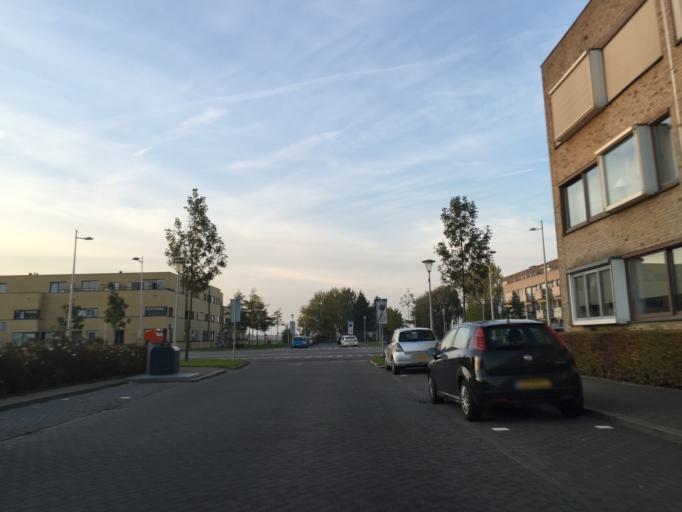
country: NL
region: South Holland
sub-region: Gemeente Lansingerland
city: Berkel en Rodenrijs
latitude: 52.0004
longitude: 4.4674
